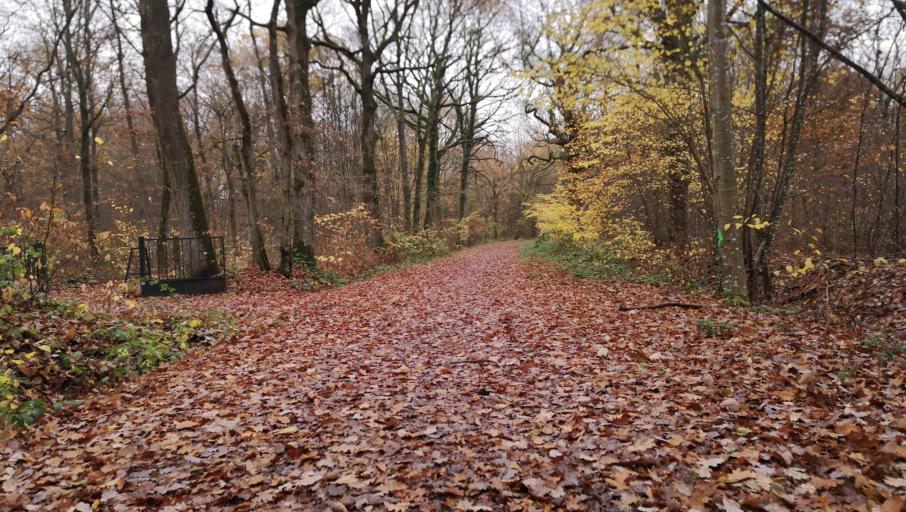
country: FR
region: Centre
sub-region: Departement du Loiret
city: Saint-Jean-de-Braye
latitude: 47.9335
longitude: 1.9848
